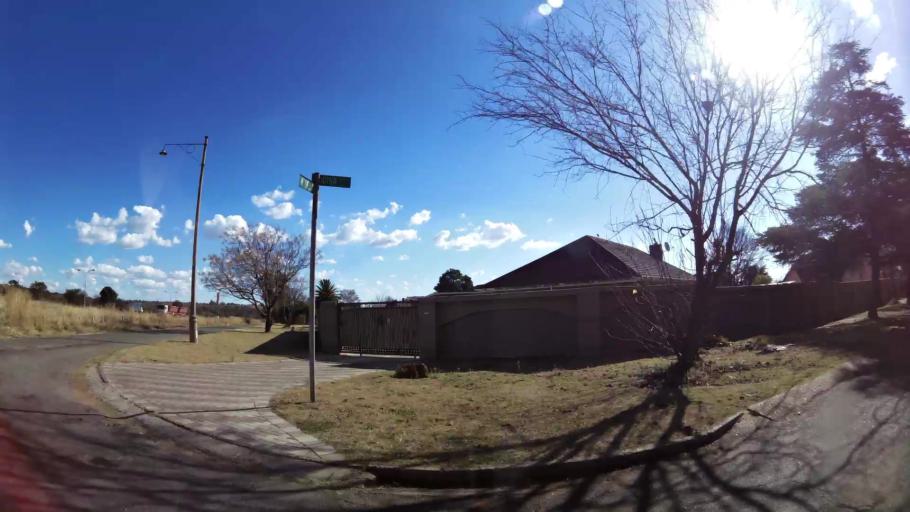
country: ZA
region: Gauteng
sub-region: West Rand District Municipality
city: Carletonville
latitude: -26.3743
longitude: 27.4043
